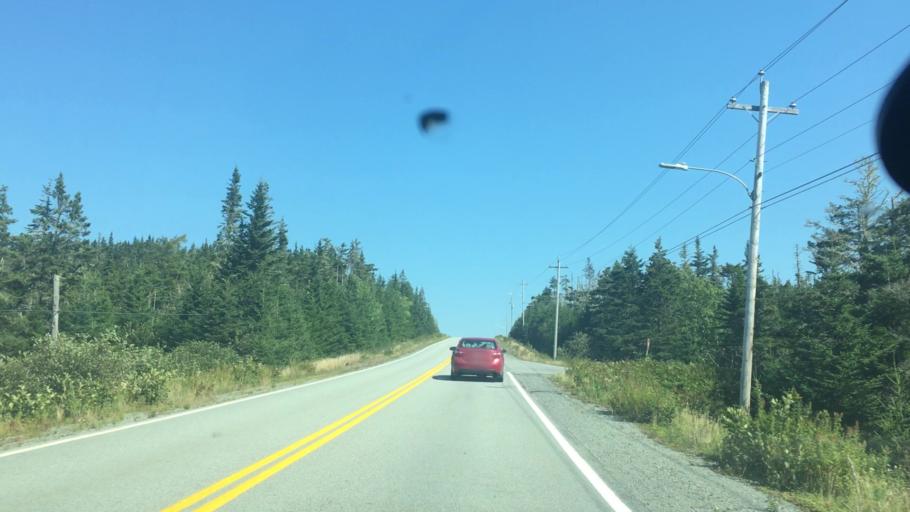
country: CA
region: Nova Scotia
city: Antigonish
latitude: 44.9371
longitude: -62.2697
